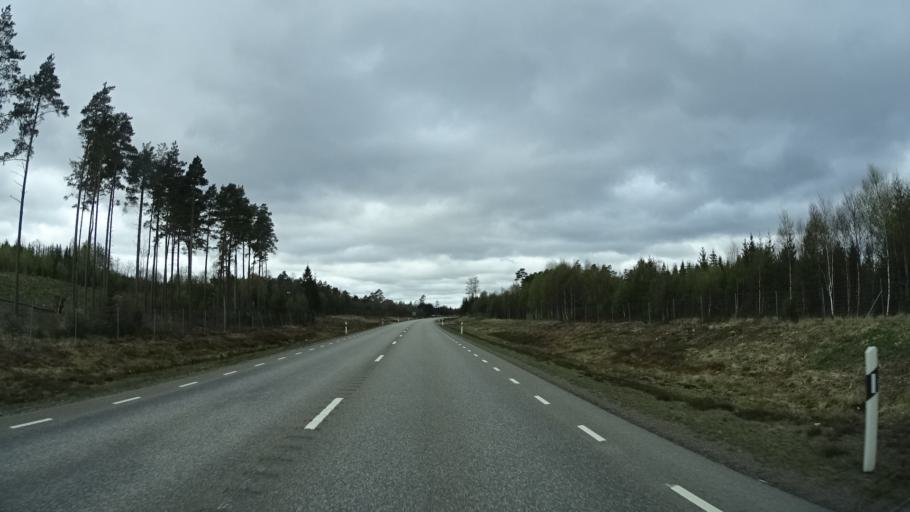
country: SE
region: Kronoberg
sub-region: Markaryds Kommun
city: Stromsnasbruk
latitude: 56.7551
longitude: 13.5691
